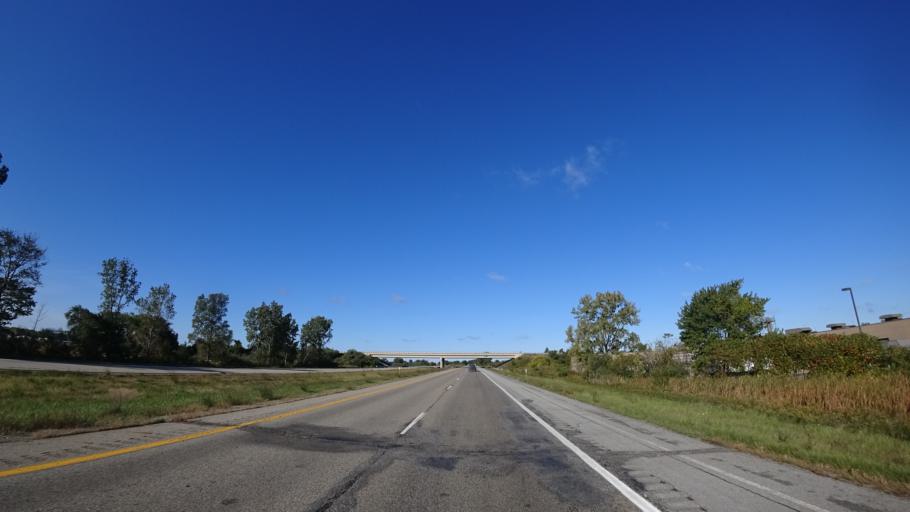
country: US
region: Michigan
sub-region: Ottawa County
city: Holland
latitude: 42.7367
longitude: -86.1132
